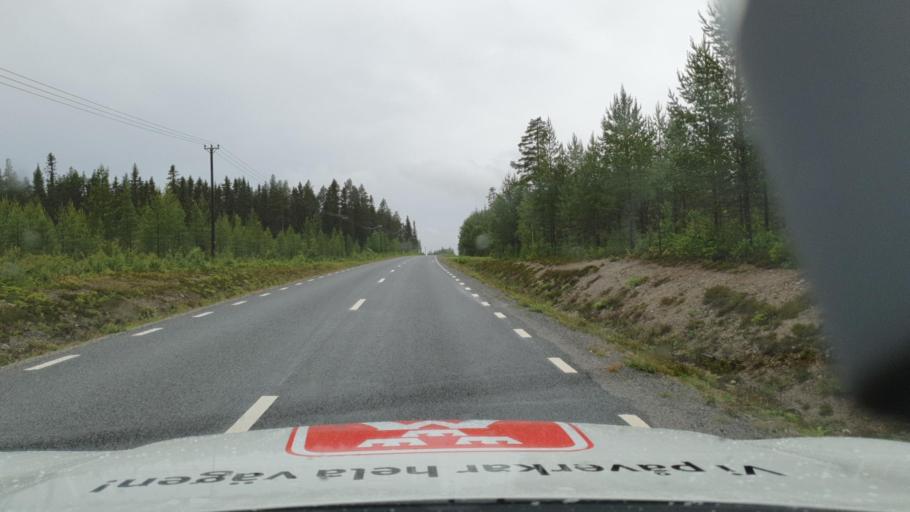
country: SE
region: Vaesterbotten
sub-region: Asele Kommun
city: Asele
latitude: 63.9172
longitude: 17.2409
